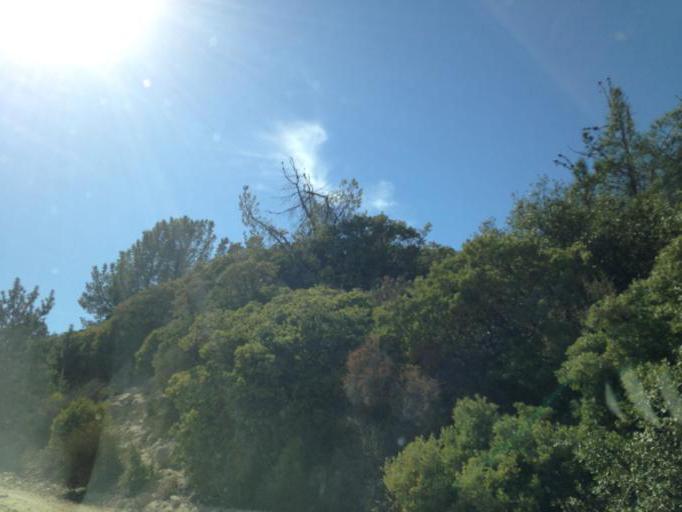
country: US
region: California
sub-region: San Bernardino County
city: Running Springs
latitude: 34.1653
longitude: -117.0788
